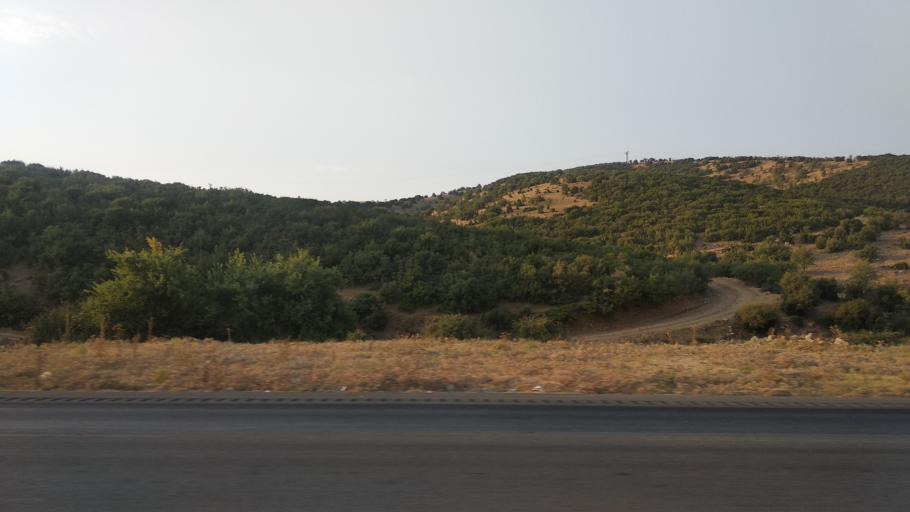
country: TR
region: Manisa
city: Menye
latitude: 38.5543
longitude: 28.4773
